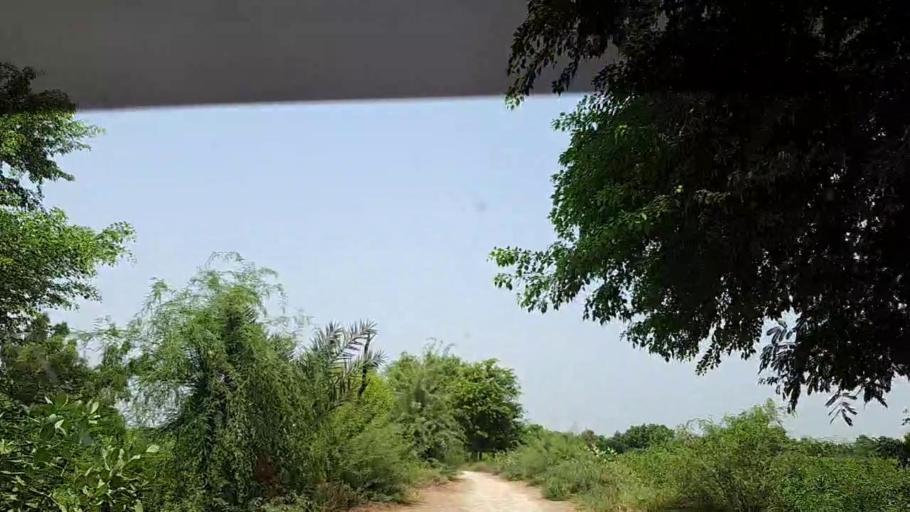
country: PK
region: Sindh
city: Adilpur
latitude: 27.8810
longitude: 69.2608
